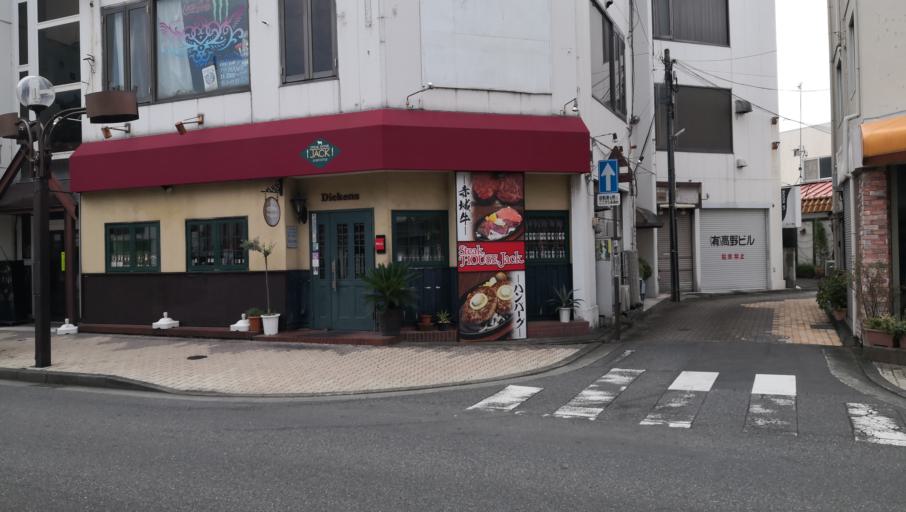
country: JP
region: Gunma
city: Maebashi-shi
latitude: 36.3924
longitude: 139.0723
